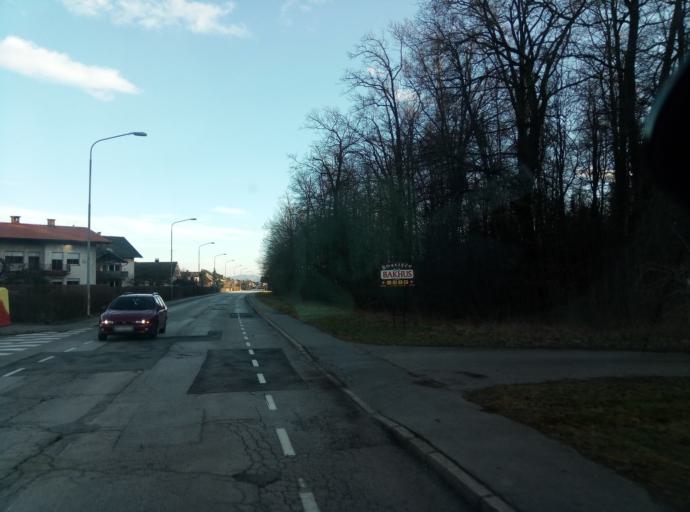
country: SI
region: Sencur
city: Hrastje
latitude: 46.2249
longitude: 14.3767
